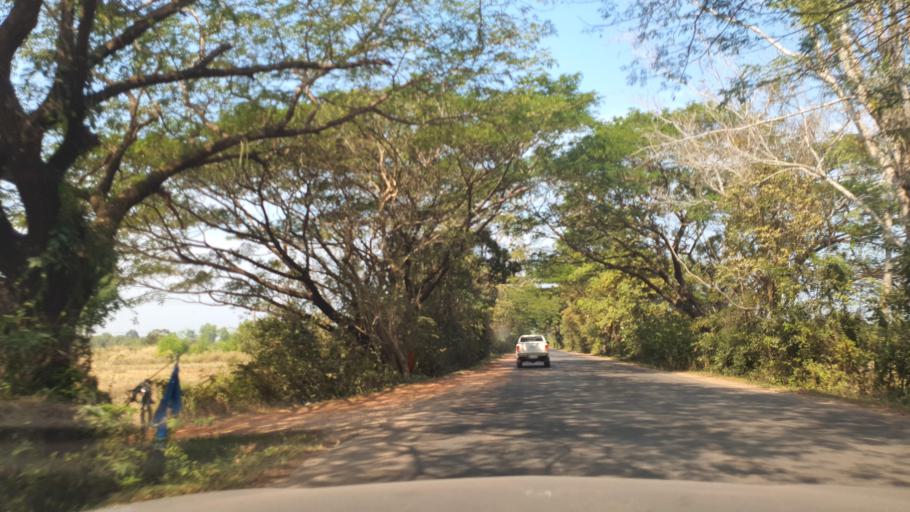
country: TH
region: Nakhon Phanom
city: Ban Phaeng
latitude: 18.0233
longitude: 104.1478
